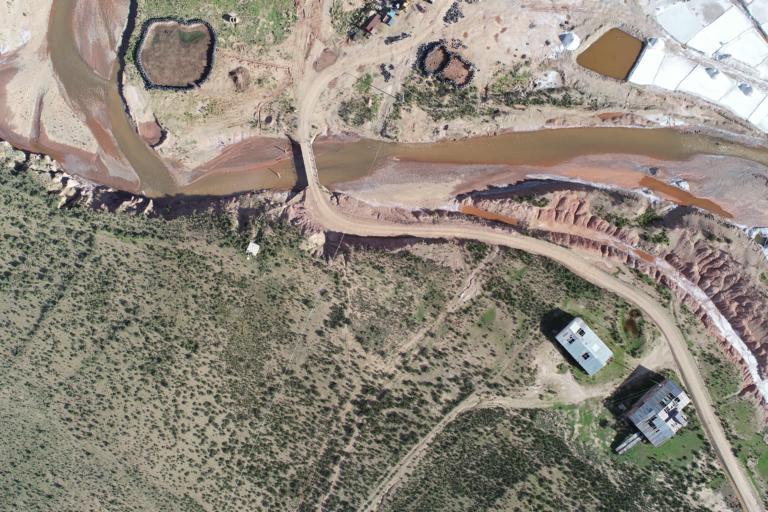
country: BO
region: La Paz
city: Patacamaya
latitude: -17.2982
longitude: -68.4835
